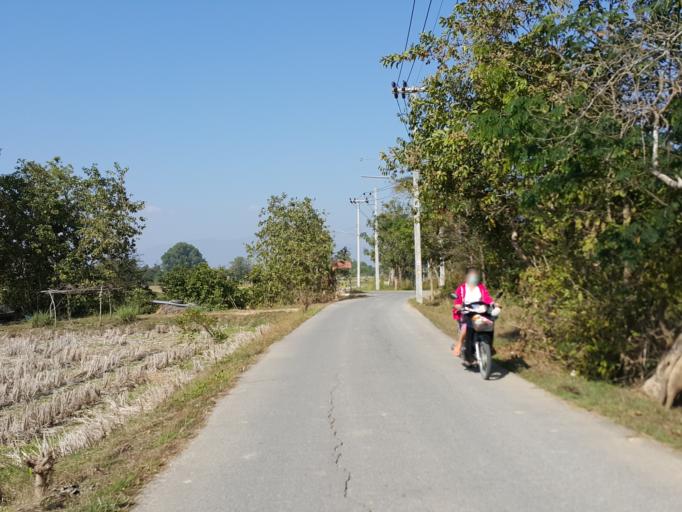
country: TH
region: Chiang Mai
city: San Kamphaeng
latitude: 18.8059
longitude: 99.0986
